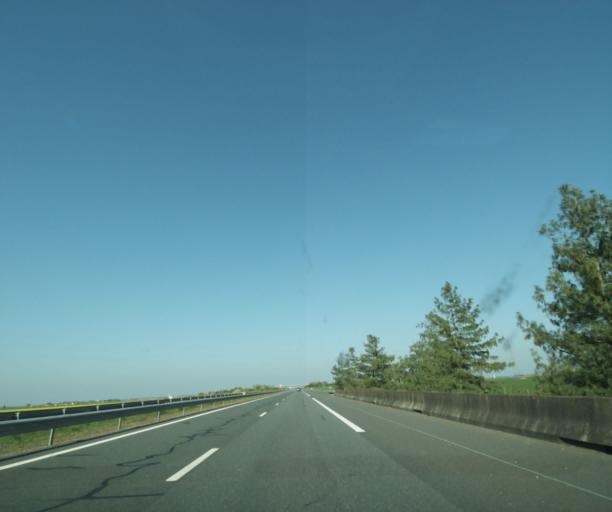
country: FR
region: Centre
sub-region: Departement du Loiret
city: Corquilleroy
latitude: 48.0883
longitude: 2.6906
